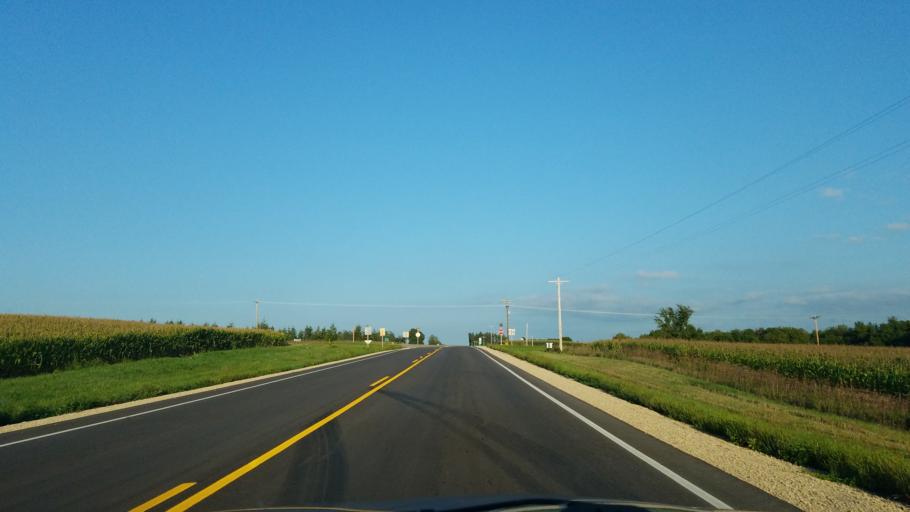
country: US
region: Wisconsin
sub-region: Saint Croix County
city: Baldwin
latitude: 45.0790
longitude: -92.3771
